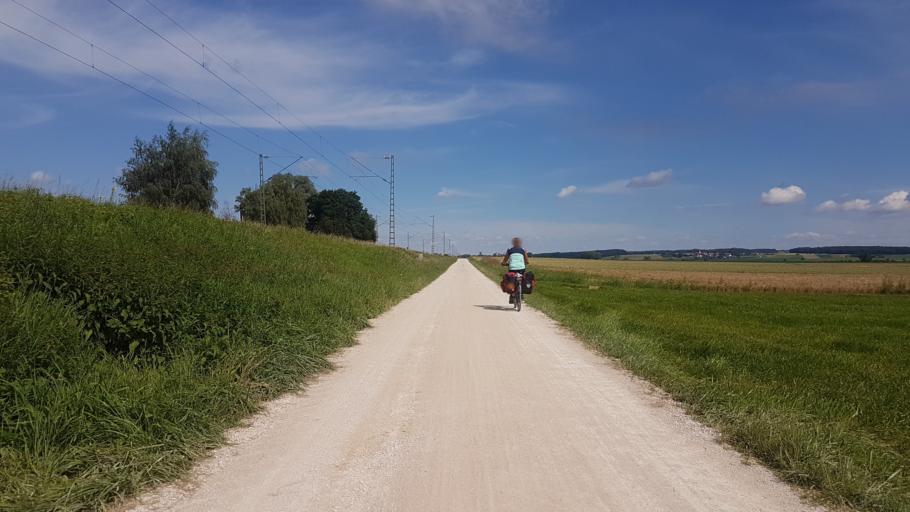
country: DE
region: Bavaria
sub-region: Regierungsbezirk Mittelfranken
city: Markt Berolzheim
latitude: 49.0244
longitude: 10.8475
